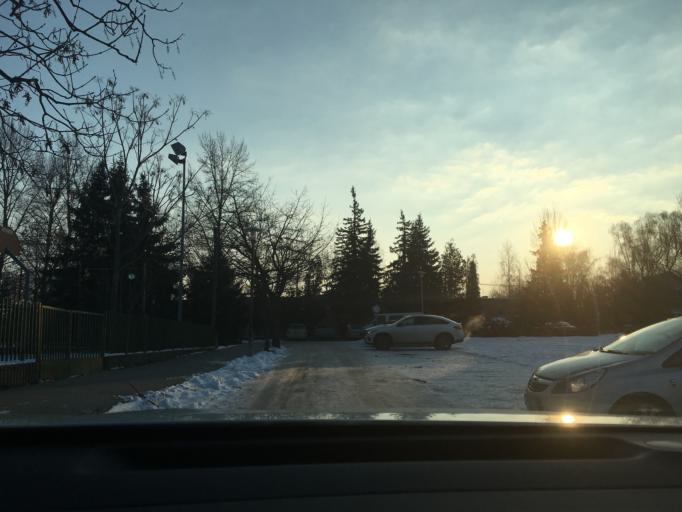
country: HU
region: Budapest
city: Budapest XVII. keruelet
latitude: 47.4706
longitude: 19.2923
